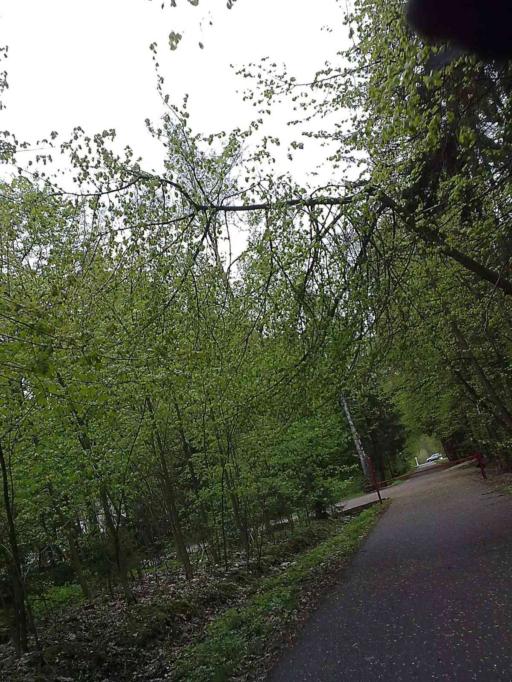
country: RU
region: Moskovskaya
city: Lesnoy Gorodok
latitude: 55.6689
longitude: 37.1694
